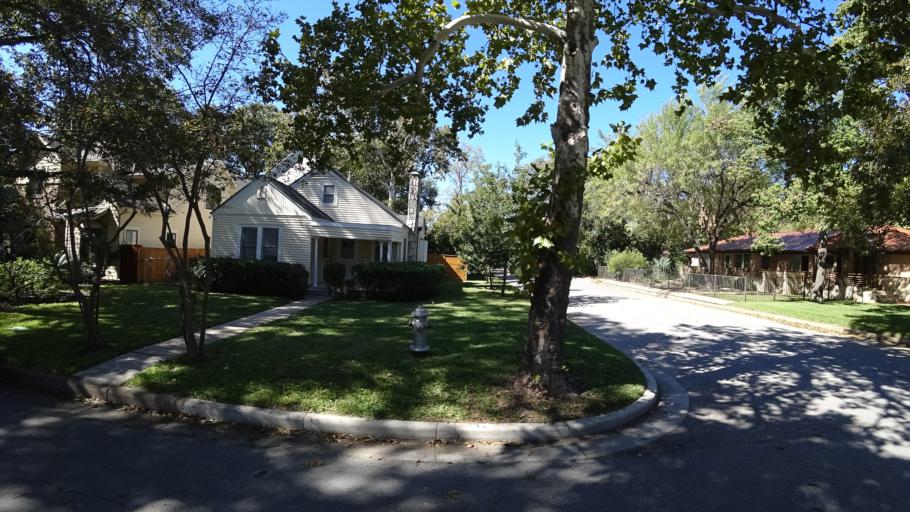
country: US
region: Texas
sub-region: Travis County
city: Austin
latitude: 30.3138
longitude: -97.7450
